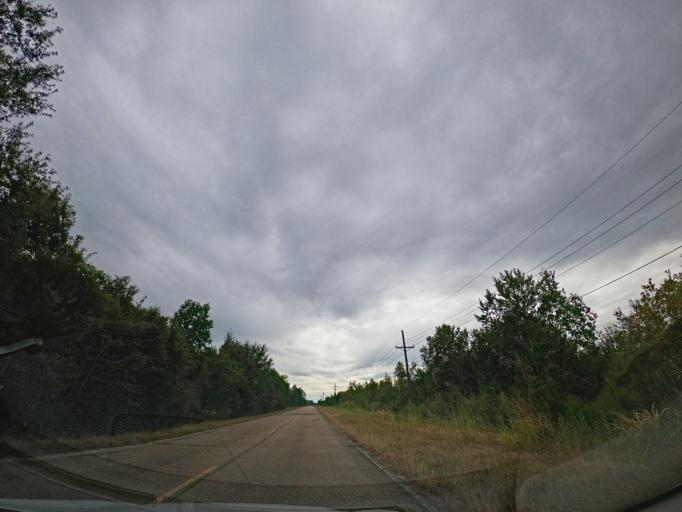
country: US
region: Mississippi
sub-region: Hancock County
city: Pearlington
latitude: 30.2169
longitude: -89.6886
